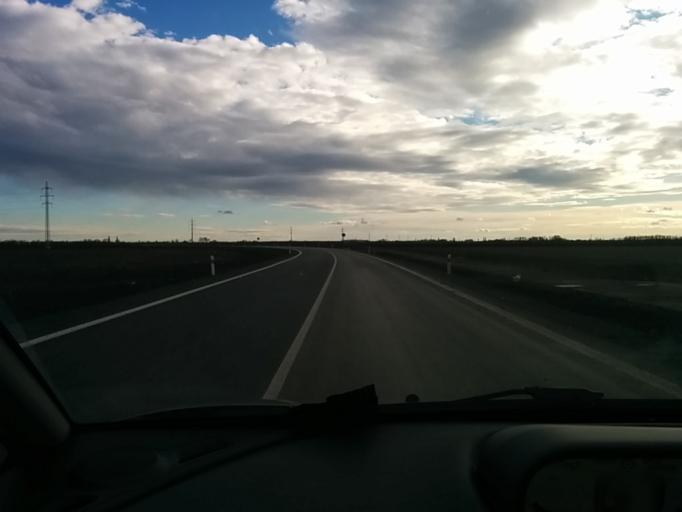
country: SK
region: Trnavsky
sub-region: Okres Galanta
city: Galanta
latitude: 48.2729
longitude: 17.6986
